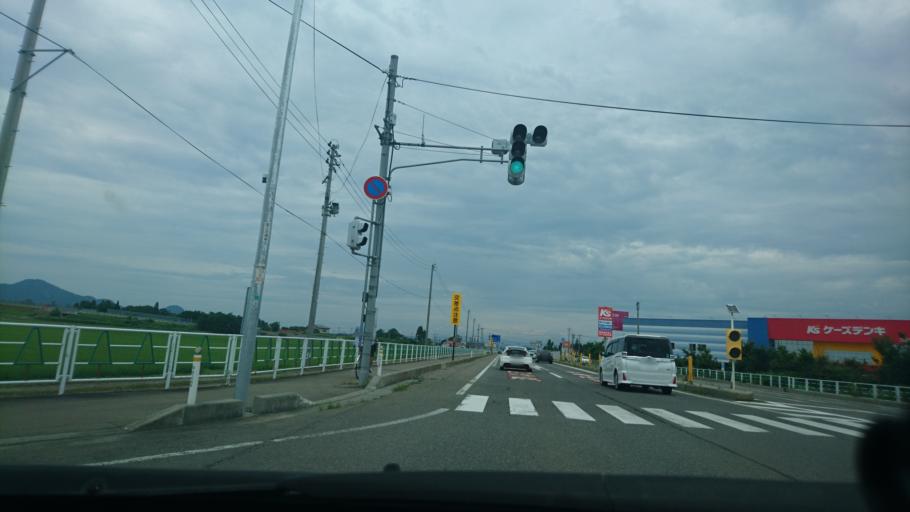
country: JP
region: Akita
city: Omagari
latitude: 39.4392
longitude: 140.5065
